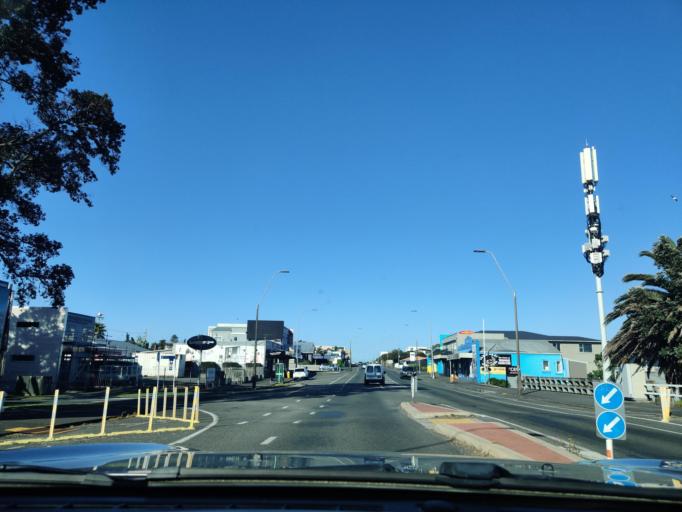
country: NZ
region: Taranaki
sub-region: New Plymouth District
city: New Plymouth
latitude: -39.0517
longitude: 174.0939
